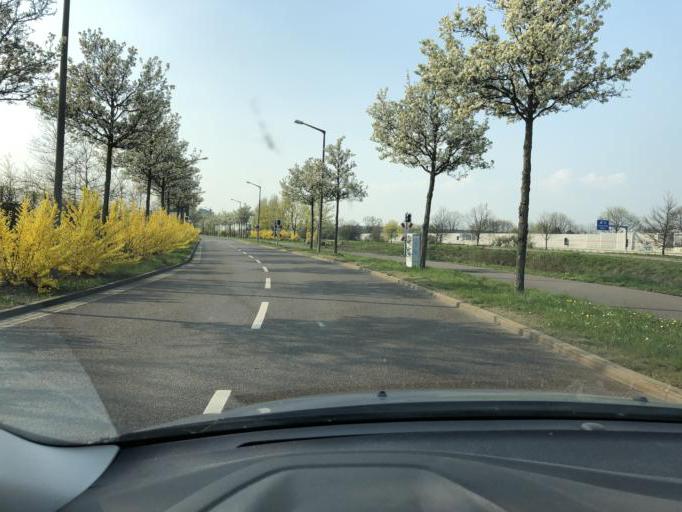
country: DE
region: Saxony
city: Rackwitz
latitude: 51.3986
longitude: 12.4128
